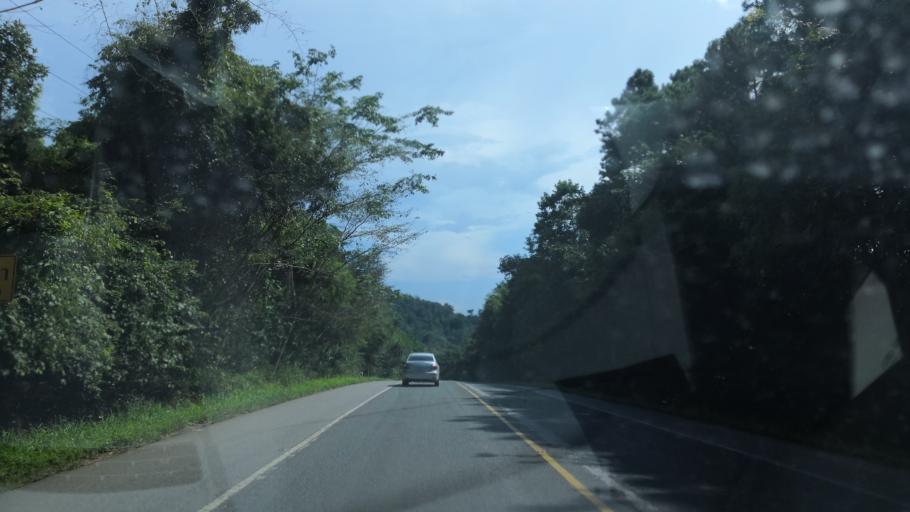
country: TH
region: Chiang Rai
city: Wiang Pa Pao
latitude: 19.4636
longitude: 99.4893
